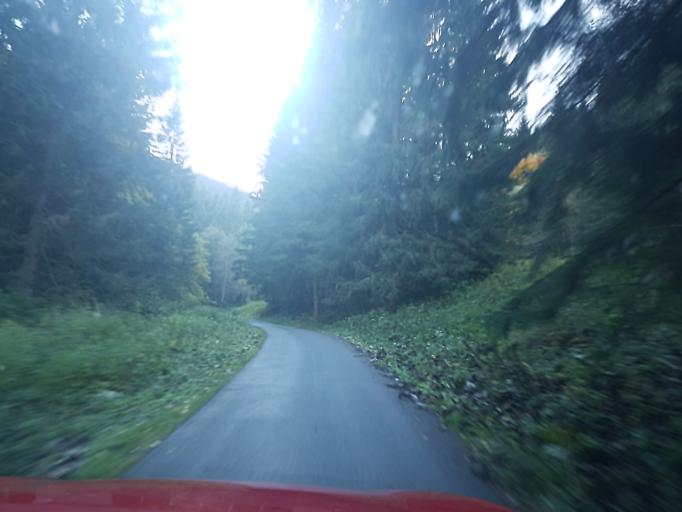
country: SK
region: Zilinsky
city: Ruzomberok
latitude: 48.9989
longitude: 19.2419
